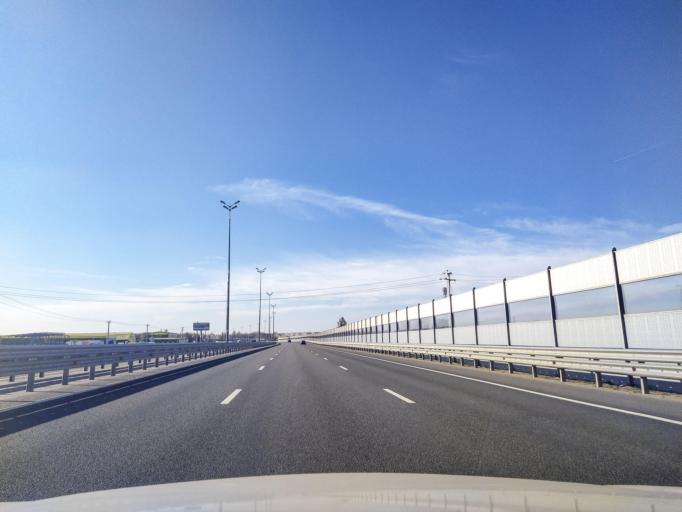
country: RU
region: Leningrad
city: Mariyenburg
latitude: 59.5255
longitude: 30.0911
